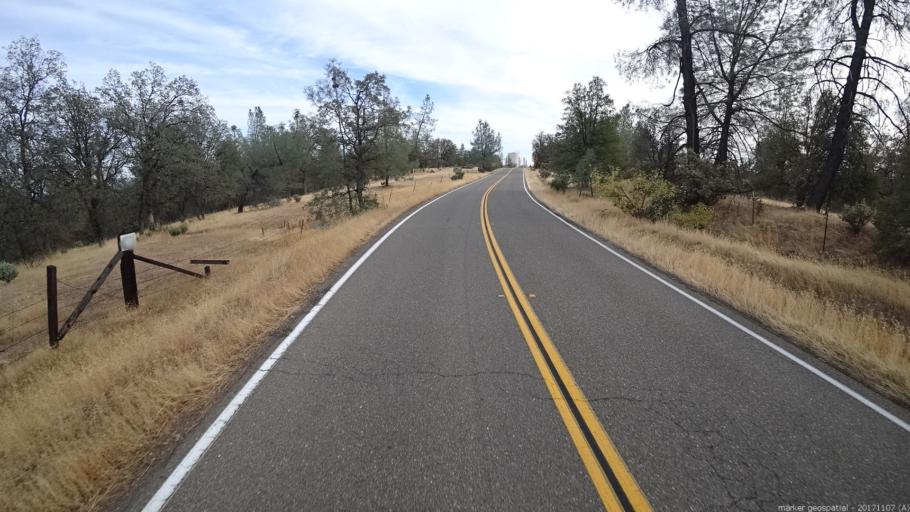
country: US
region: California
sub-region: Shasta County
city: Shasta
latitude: 40.4946
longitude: -122.5181
